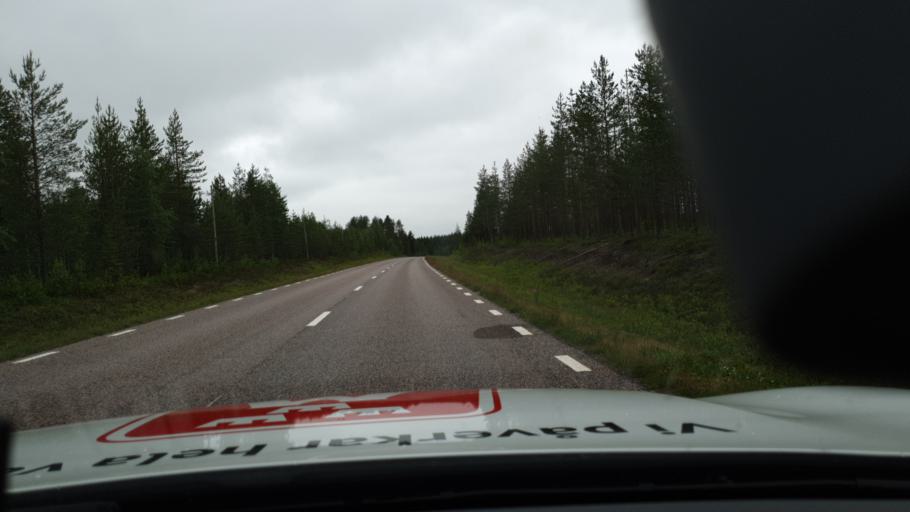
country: FI
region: Lapland
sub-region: Tunturi-Lappi
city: Kolari
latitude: 67.0414
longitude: 23.6927
